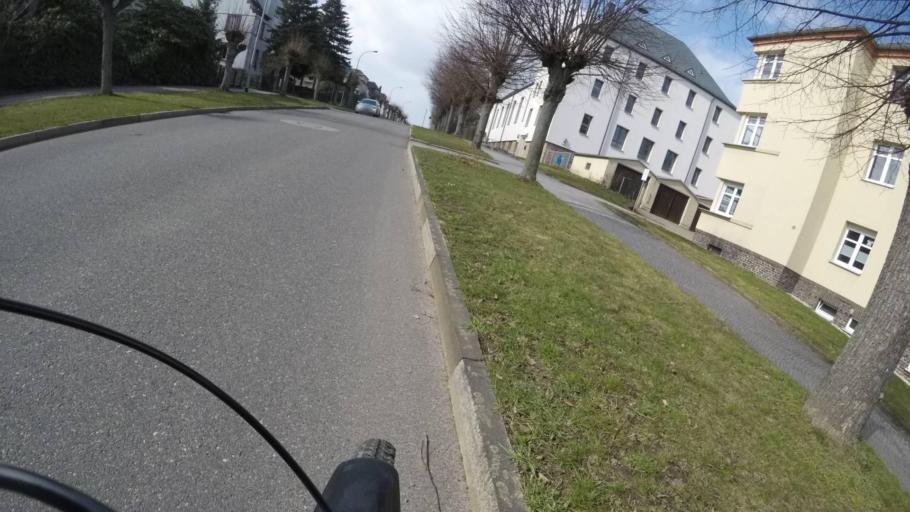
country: DE
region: Saxony
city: Limbach-Oberfrohna
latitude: 50.8625
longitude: 12.7383
